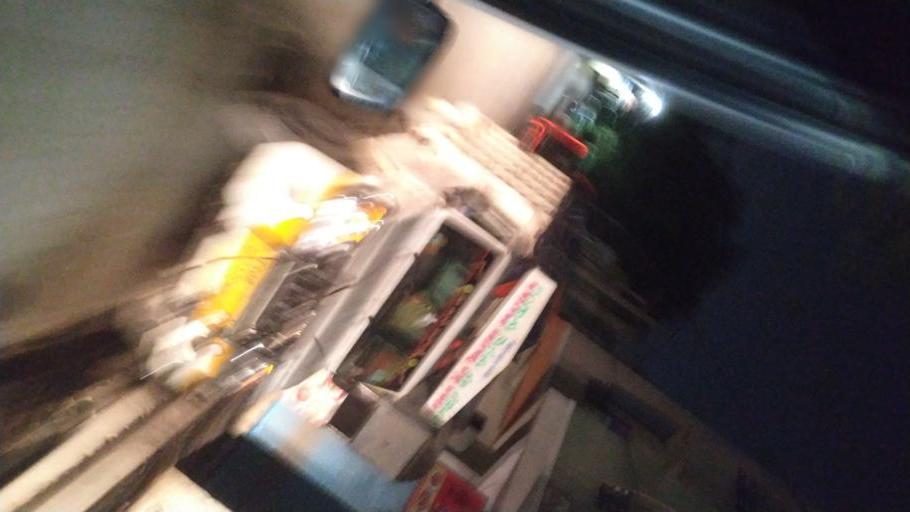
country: IN
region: Telangana
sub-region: Rangareddi
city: Quthbullapur
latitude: 17.4963
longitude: 78.4449
